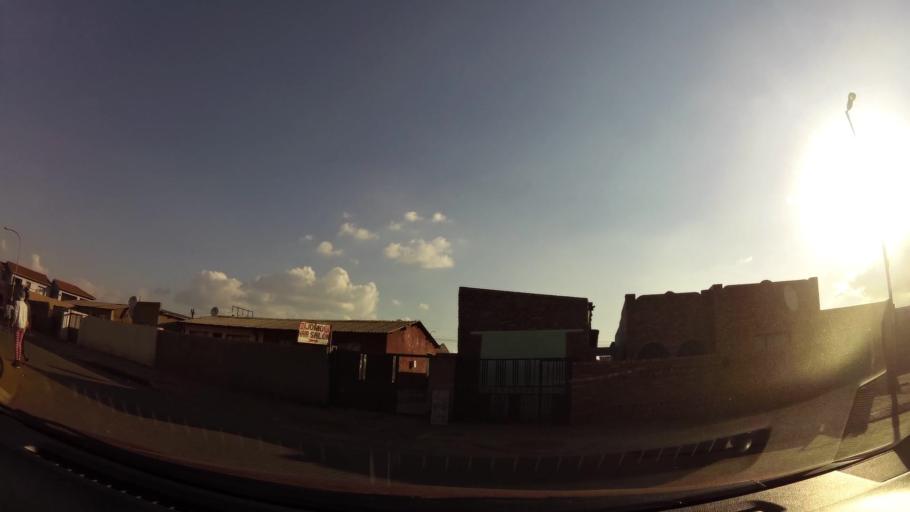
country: ZA
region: Gauteng
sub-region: City of Johannesburg Metropolitan Municipality
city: Soweto
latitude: -26.2273
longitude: 27.8591
